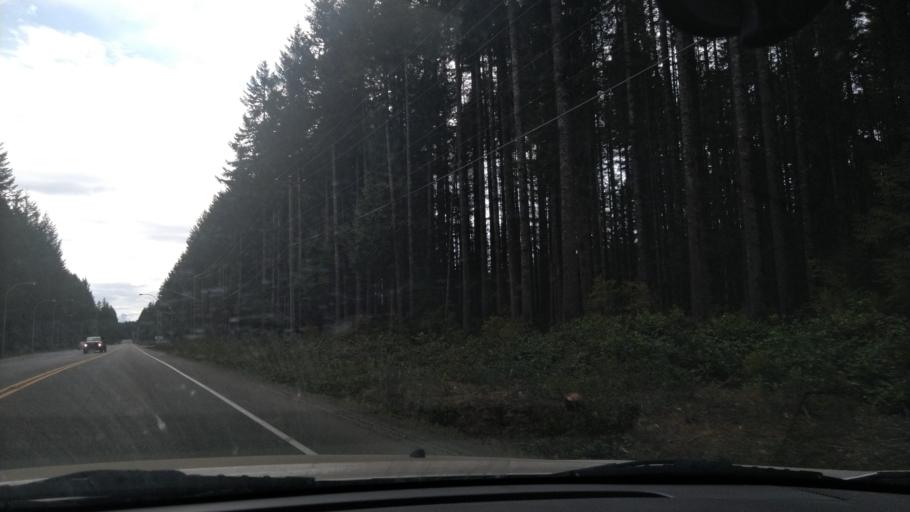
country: CA
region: British Columbia
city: Campbell River
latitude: 50.0200
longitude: -125.3534
